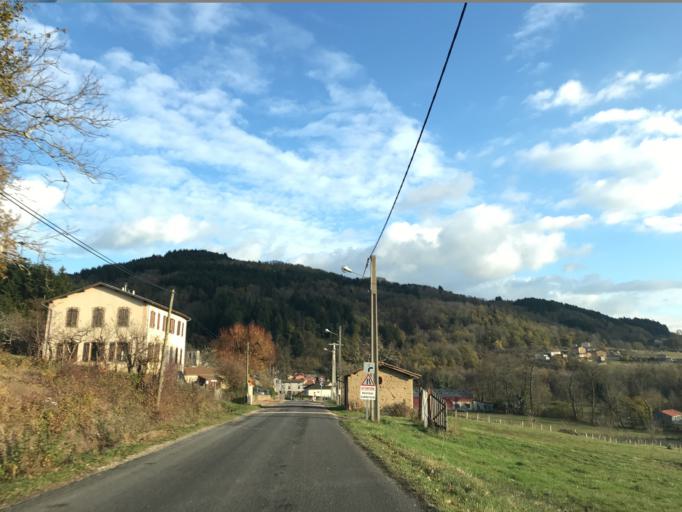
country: FR
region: Auvergne
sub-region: Departement du Puy-de-Dome
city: Courpiere
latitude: 45.7560
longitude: 3.6133
